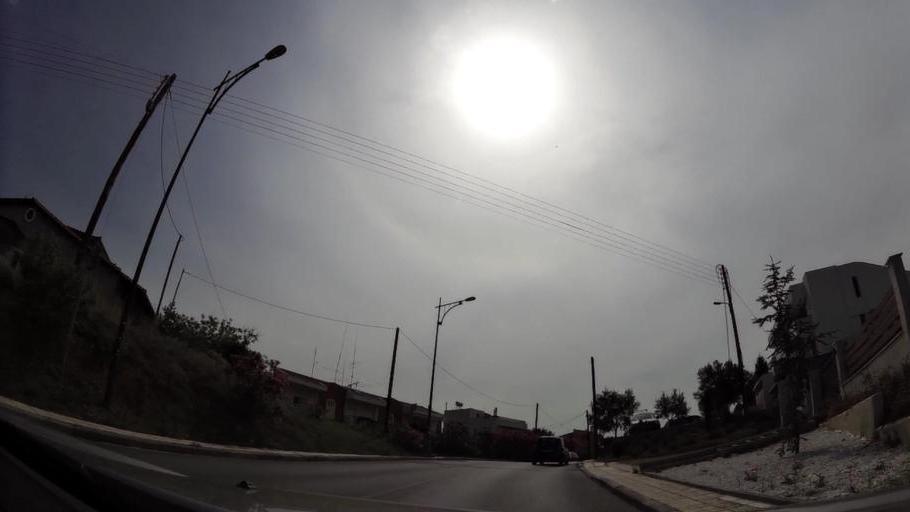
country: GR
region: Central Macedonia
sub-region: Nomos Thessalonikis
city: Panorama
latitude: 40.5796
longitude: 23.0112
